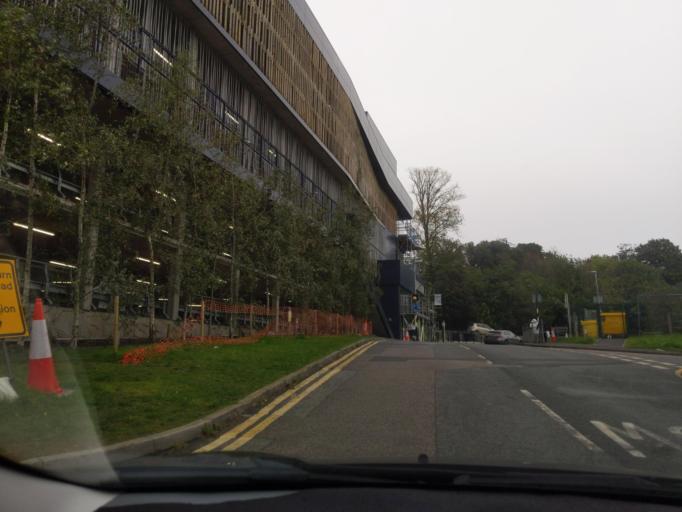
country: GB
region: England
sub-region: Plymouth
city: Plymouth
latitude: 50.4160
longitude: -4.1172
